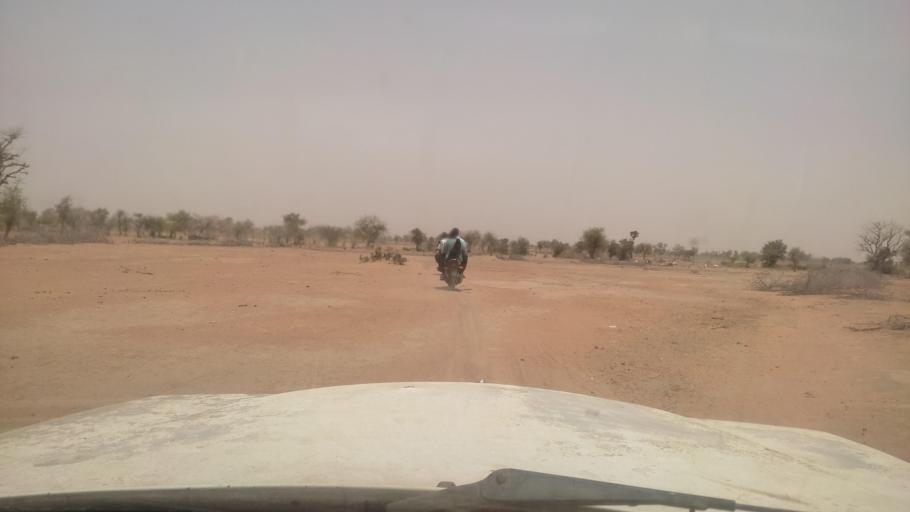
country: BF
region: Est
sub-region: Gnagna Province
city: Bogande
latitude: 13.0378
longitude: -0.0712
